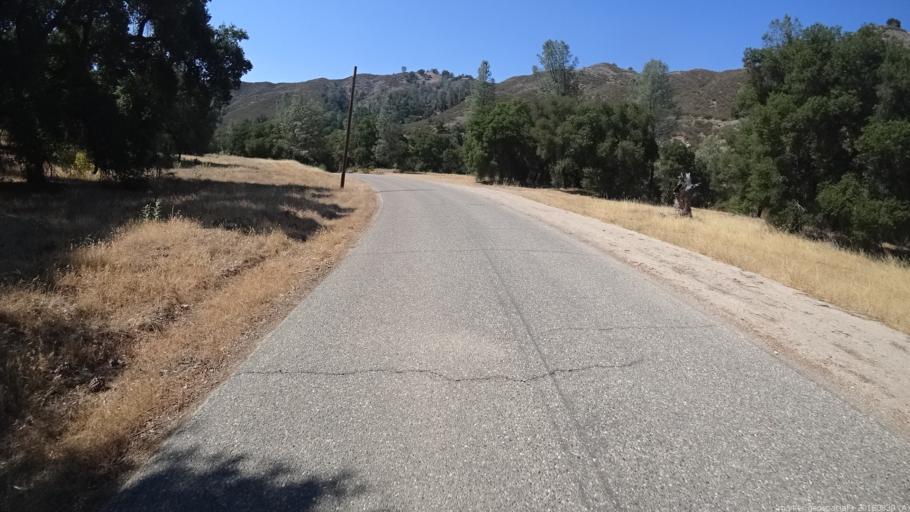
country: US
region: California
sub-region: Monterey County
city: King City
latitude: 36.0710
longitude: -121.3190
